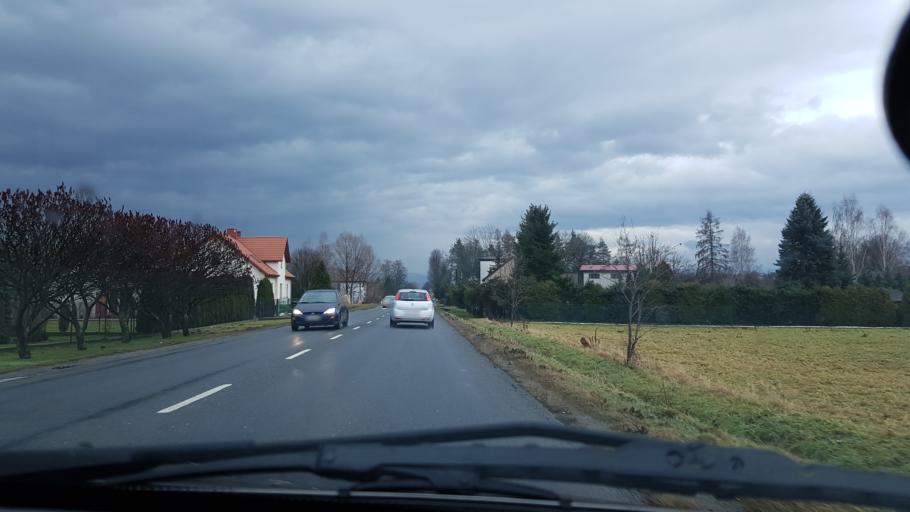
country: PL
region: Silesian Voivodeship
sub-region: Powiat zywiecki
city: Lodygowice
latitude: 49.7170
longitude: 19.1544
